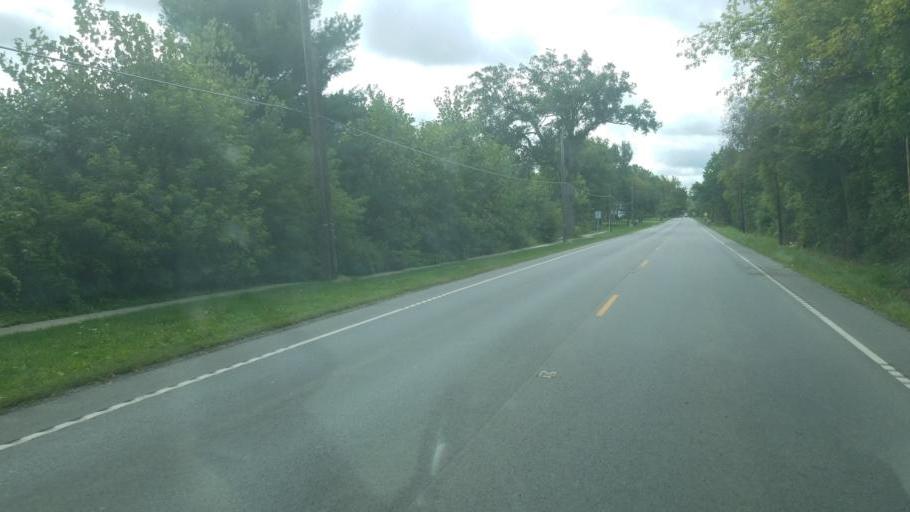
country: US
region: Ohio
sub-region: Lorain County
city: Oberlin
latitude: 41.3052
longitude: -82.2170
